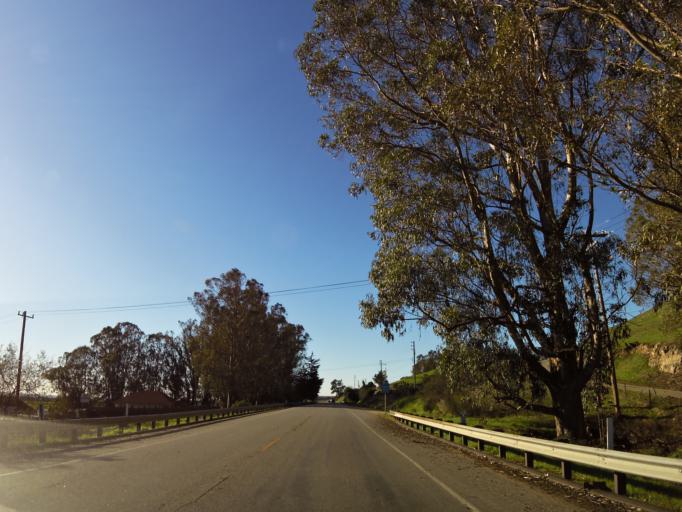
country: US
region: California
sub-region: Santa Cruz County
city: Santa Cruz
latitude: 36.9618
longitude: -122.0681
